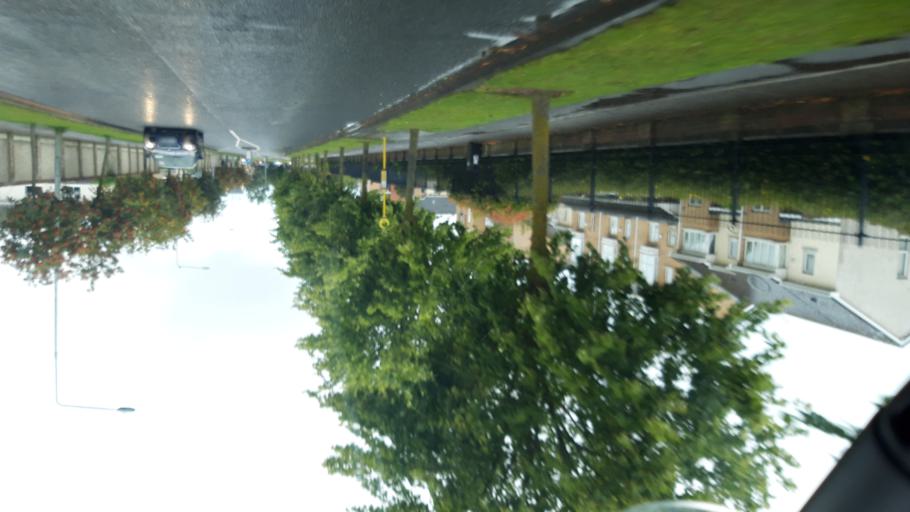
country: IE
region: Leinster
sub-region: Fingal County
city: Blanchardstown
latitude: 53.3741
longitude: -6.4015
